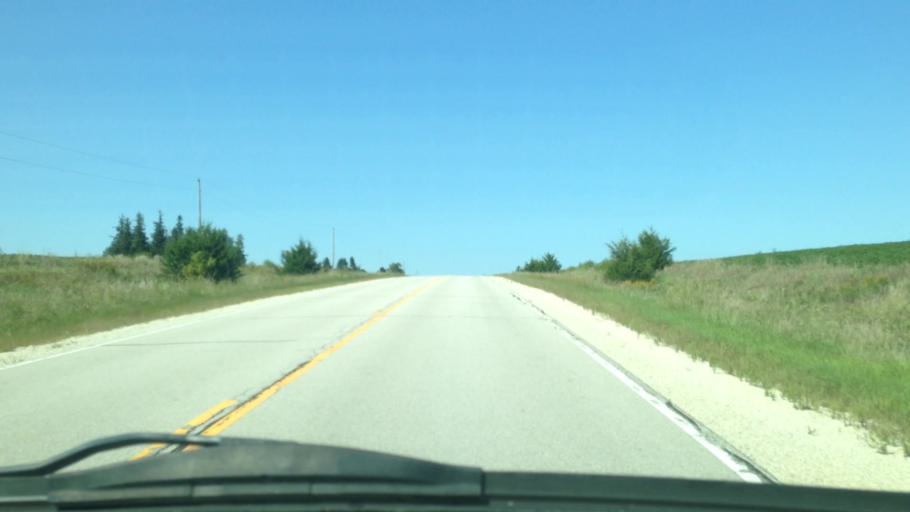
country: US
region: Minnesota
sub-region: Houston County
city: Spring Grove
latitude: 43.6356
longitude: -91.7903
